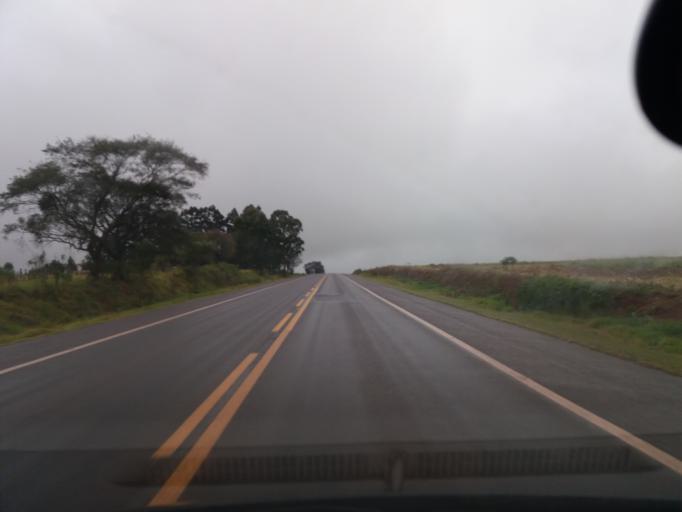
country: BR
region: Parana
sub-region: Campo Mourao
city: Campo Mourao
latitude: -24.2995
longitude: -52.5882
